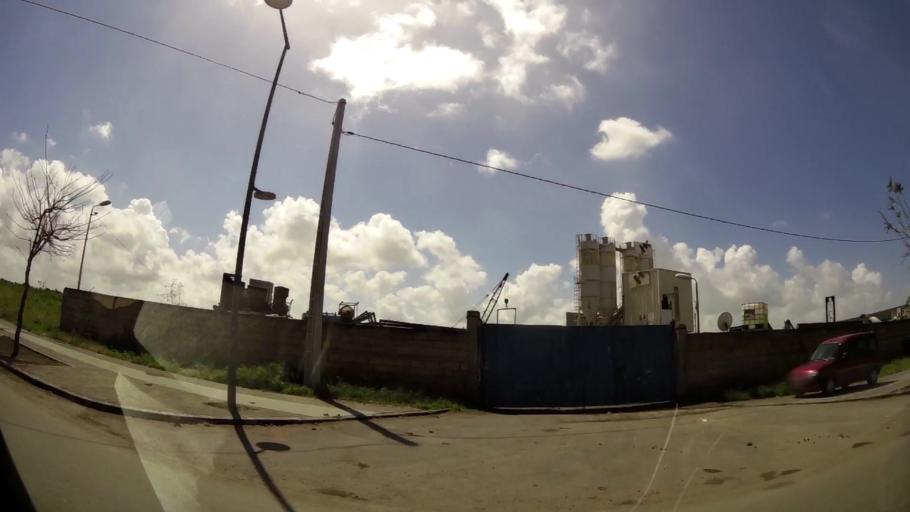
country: MA
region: Grand Casablanca
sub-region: Mediouna
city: Tit Mellil
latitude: 33.6333
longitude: -7.4669
